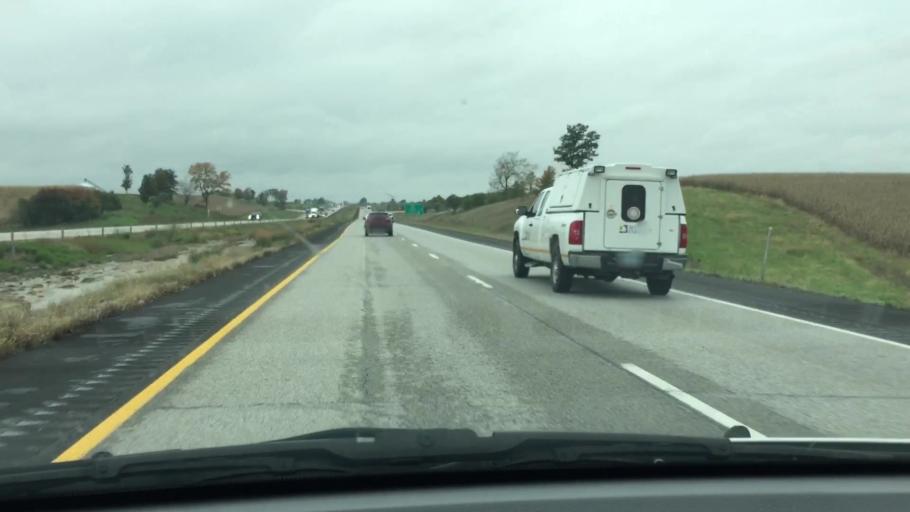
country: US
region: Iowa
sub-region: Johnson County
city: Tiffin
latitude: 41.6877
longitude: -91.7920
